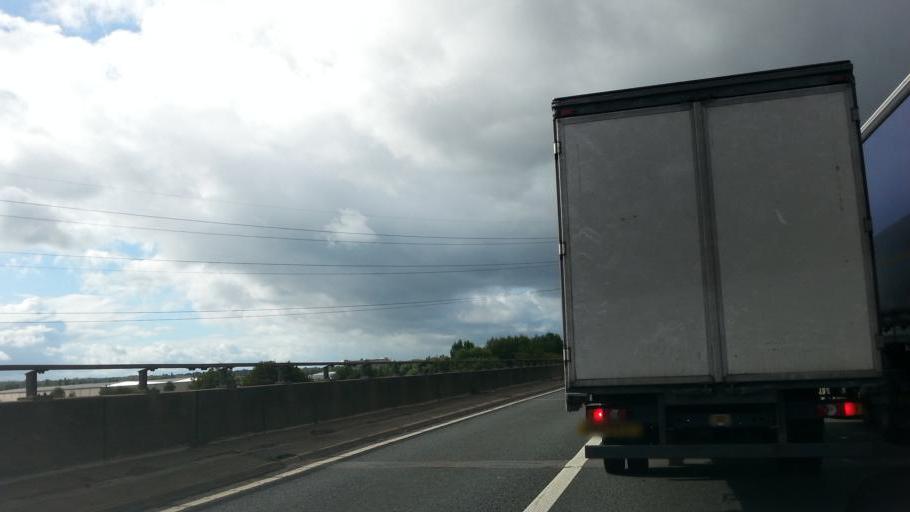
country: GB
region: England
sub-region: City and Borough of Birmingham
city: Hockley
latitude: 52.5210
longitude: -1.8781
